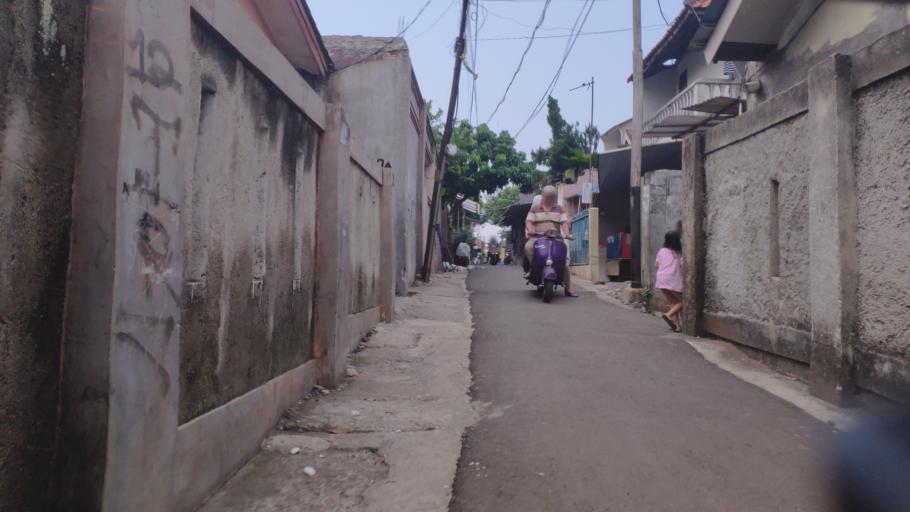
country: ID
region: West Java
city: Pamulang
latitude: -6.3113
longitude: 106.7986
